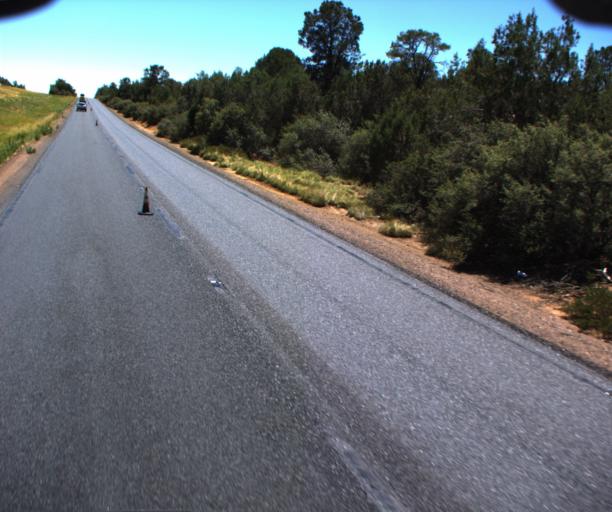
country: US
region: Arizona
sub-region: Gila County
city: Payson
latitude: 34.2090
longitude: -111.3317
